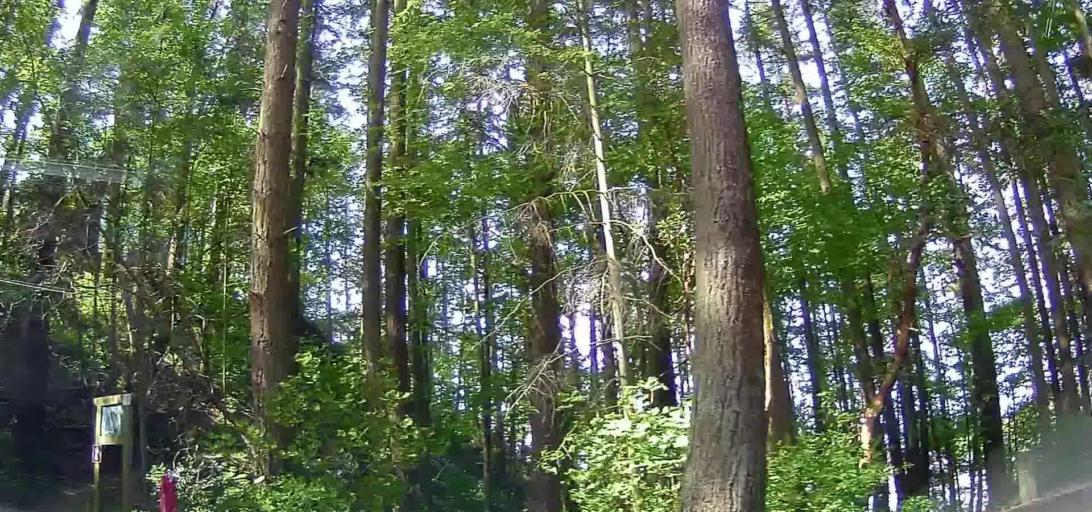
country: US
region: Washington
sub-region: Skagit County
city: Mount Vernon
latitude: 48.3849
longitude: -122.4999
